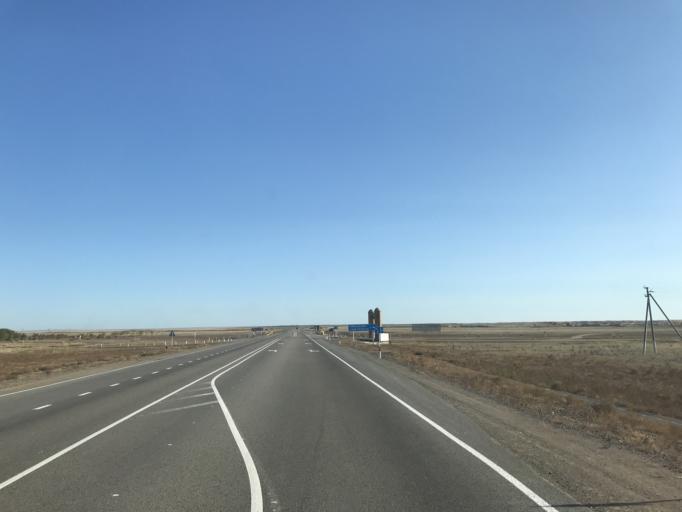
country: KZ
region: Pavlodar
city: Koktobe
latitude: 51.8981
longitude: 77.3904
